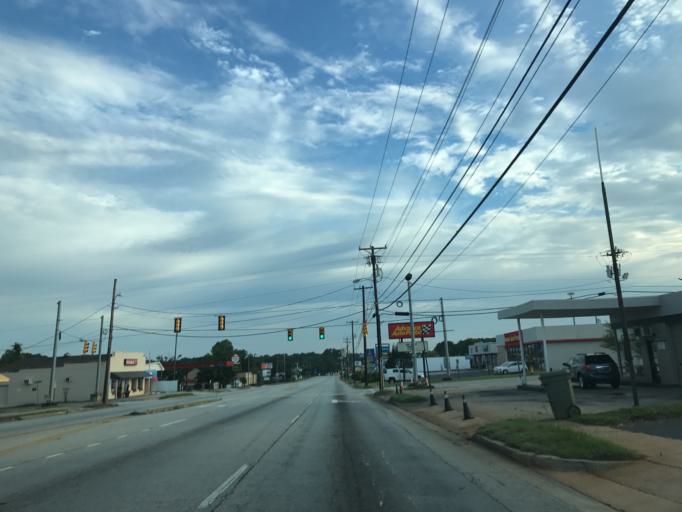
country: US
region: South Carolina
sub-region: Greenville County
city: Mauldin
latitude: 34.7821
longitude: -82.3115
